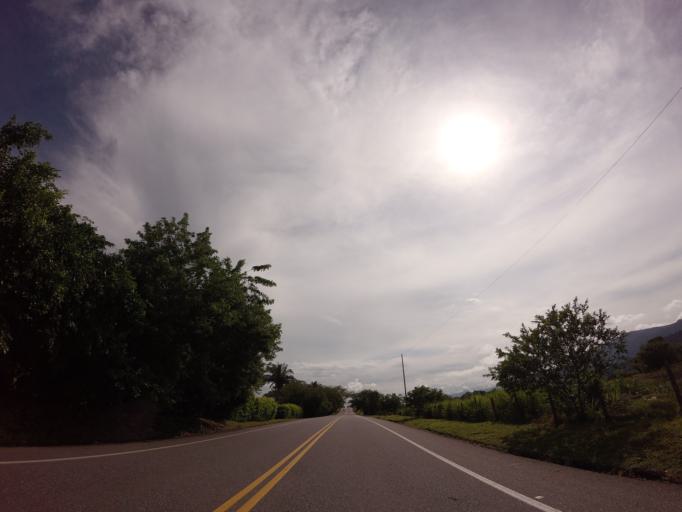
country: CO
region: Tolima
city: Honda
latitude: 5.3012
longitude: -74.7424
